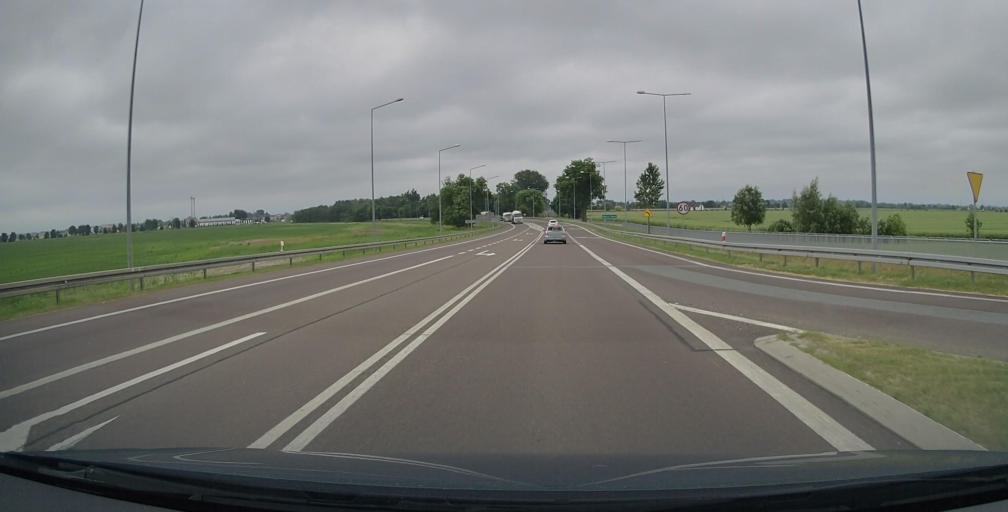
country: PL
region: Lublin Voivodeship
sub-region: Powiat bialski
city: Miedzyrzec Podlaski
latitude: 52.0023
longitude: 22.7549
